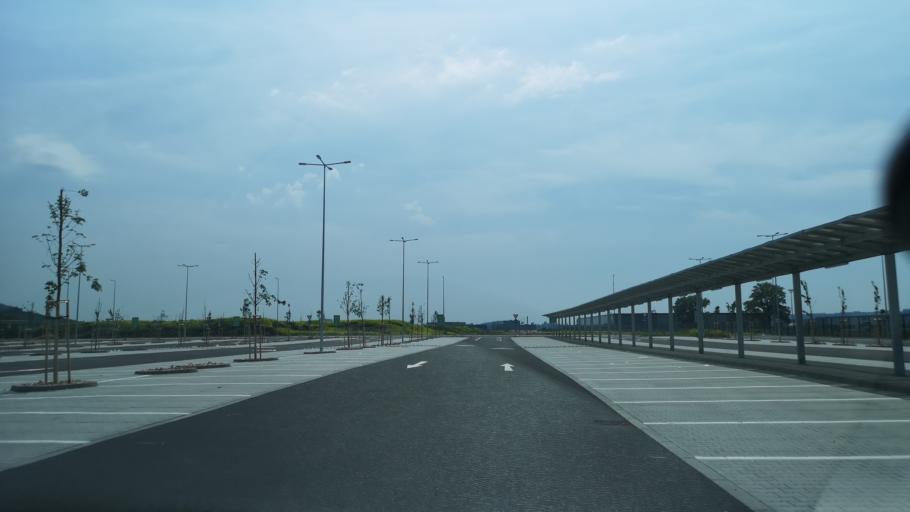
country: SK
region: Nitriansky
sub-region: Okres Nitra
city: Nitra
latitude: 48.3450
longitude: 18.0526
